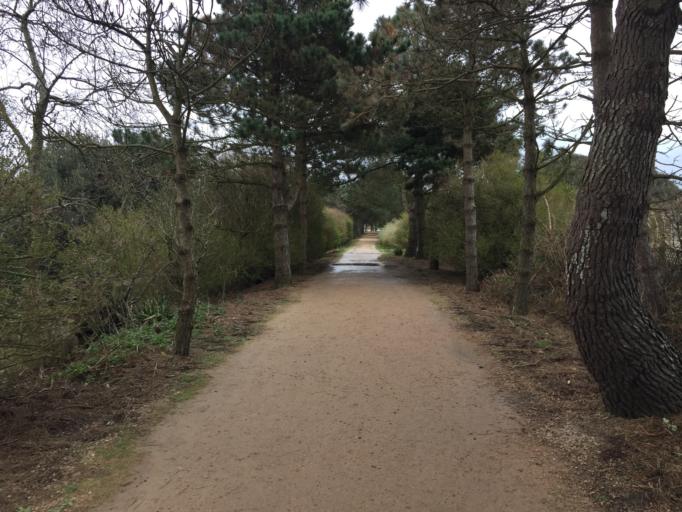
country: JE
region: St Helier
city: Saint Helier
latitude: 49.1818
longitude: -2.2335
